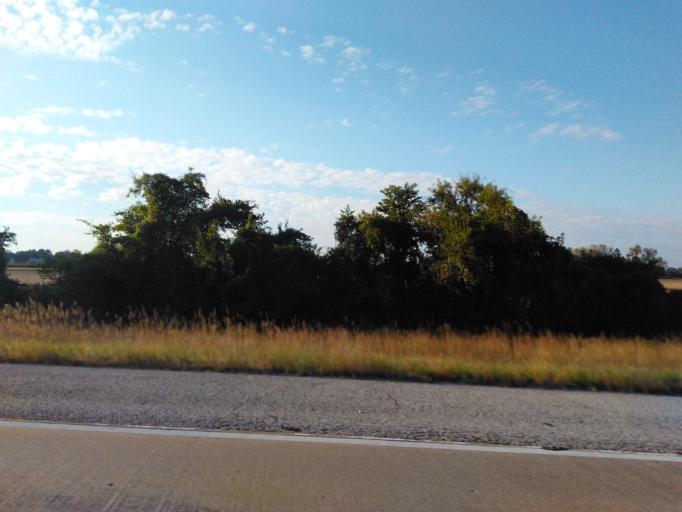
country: US
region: Illinois
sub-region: Monroe County
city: Columbia
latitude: 38.4763
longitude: -90.2268
